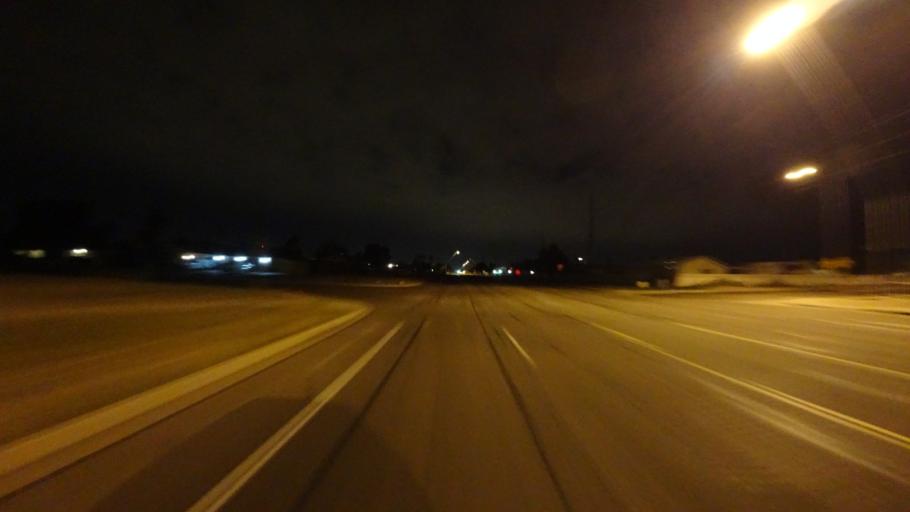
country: US
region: Arizona
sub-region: Pinal County
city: Apache Junction
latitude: 33.4223
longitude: -111.6407
